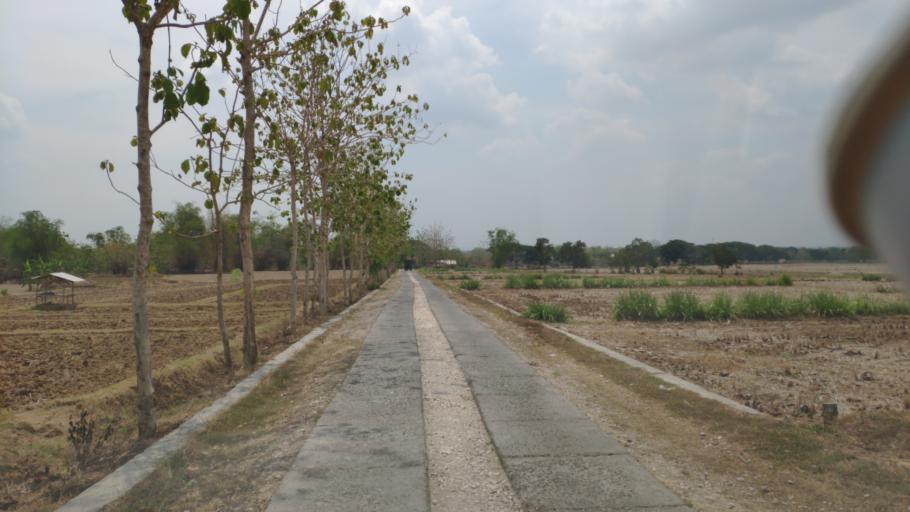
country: ID
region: Central Java
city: Berbak
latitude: -6.9967
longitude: 111.3180
